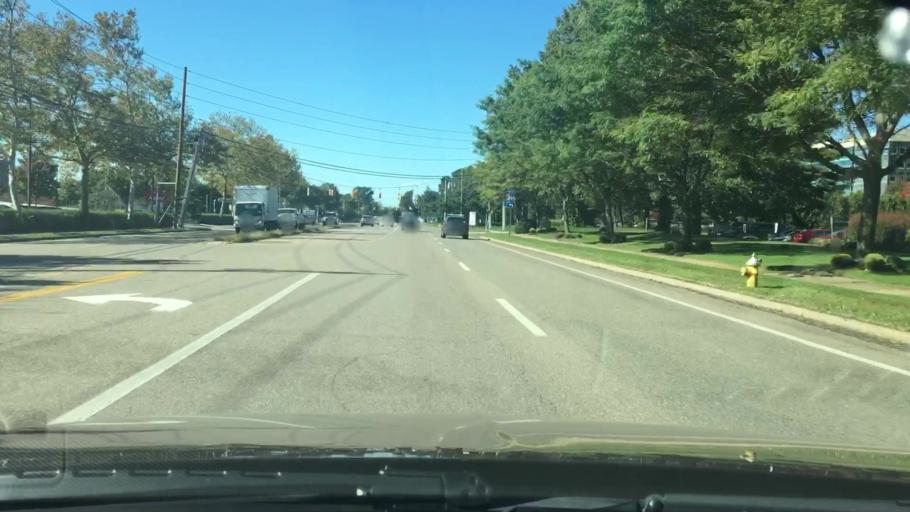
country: US
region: New York
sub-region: Suffolk County
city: Brentwood
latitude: 40.8061
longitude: -73.2645
